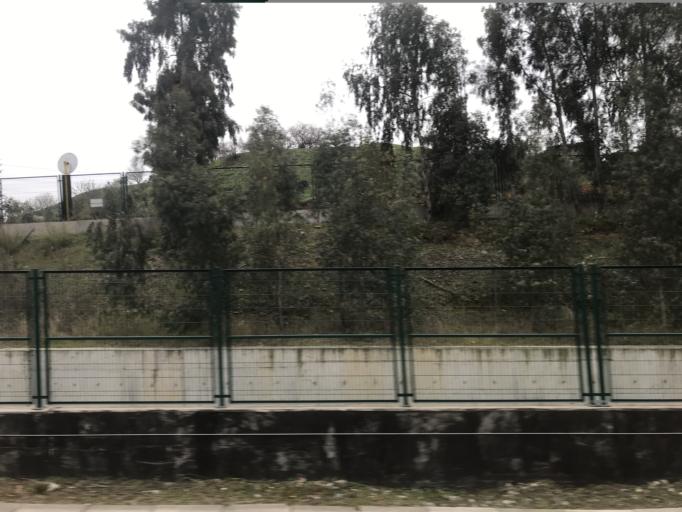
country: TR
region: Kocaeli
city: Darica
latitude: 40.8059
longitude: 29.3695
